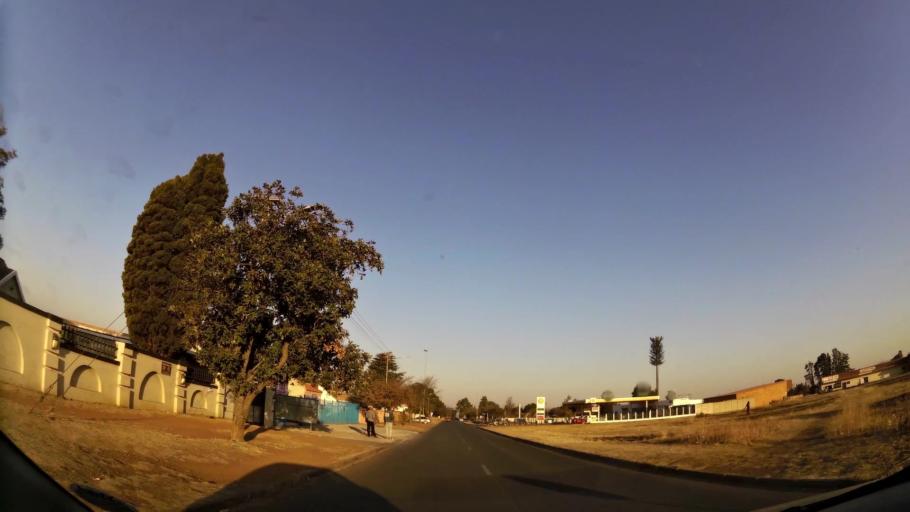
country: ZA
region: Gauteng
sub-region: West Rand District Municipality
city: Randfontein
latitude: -26.2084
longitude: 27.6555
